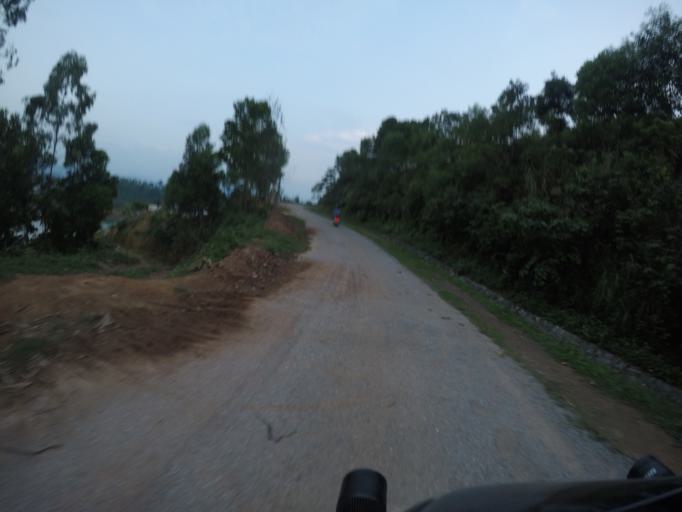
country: VN
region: Thai Nguyen
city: Chua Hang
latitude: 21.5836
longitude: 105.7095
